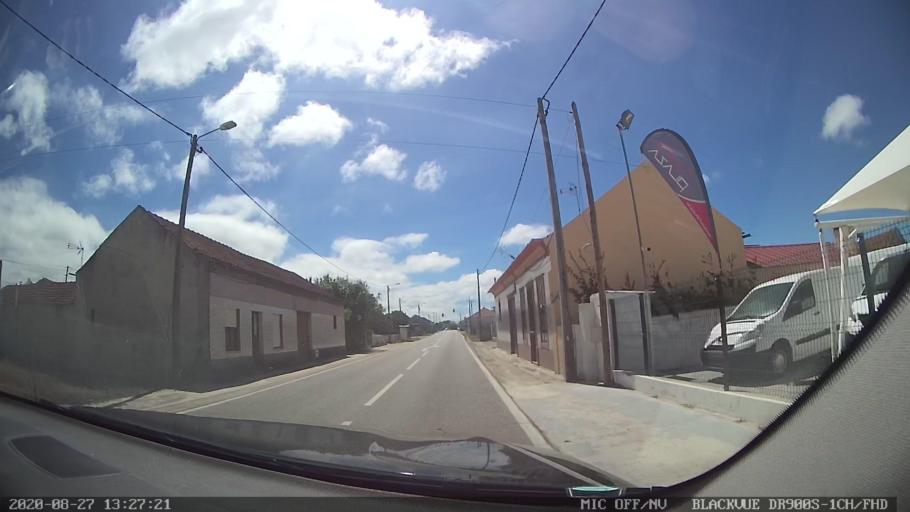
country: PT
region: Aveiro
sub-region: Vagos
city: Vagos
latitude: 40.5315
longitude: -8.6783
